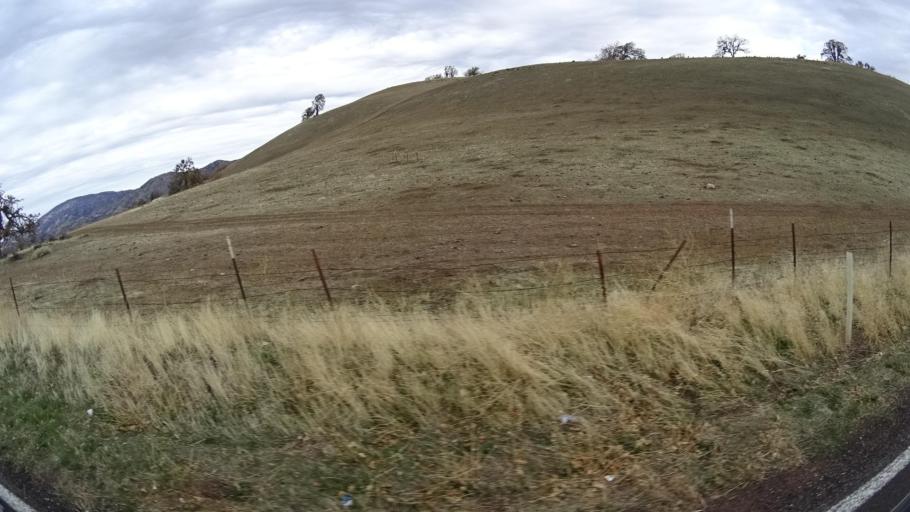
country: US
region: California
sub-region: Kern County
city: Golden Hills
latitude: 35.0947
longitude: -118.5508
